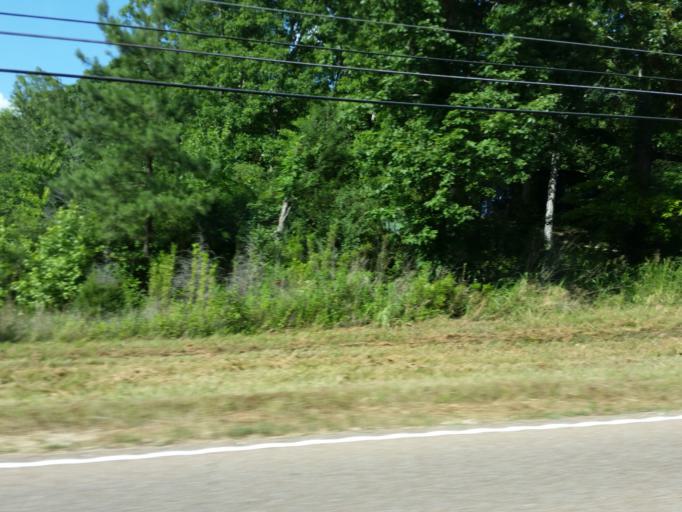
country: US
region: Tennessee
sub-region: Decatur County
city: Parsons
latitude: 35.6454
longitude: -88.1018
